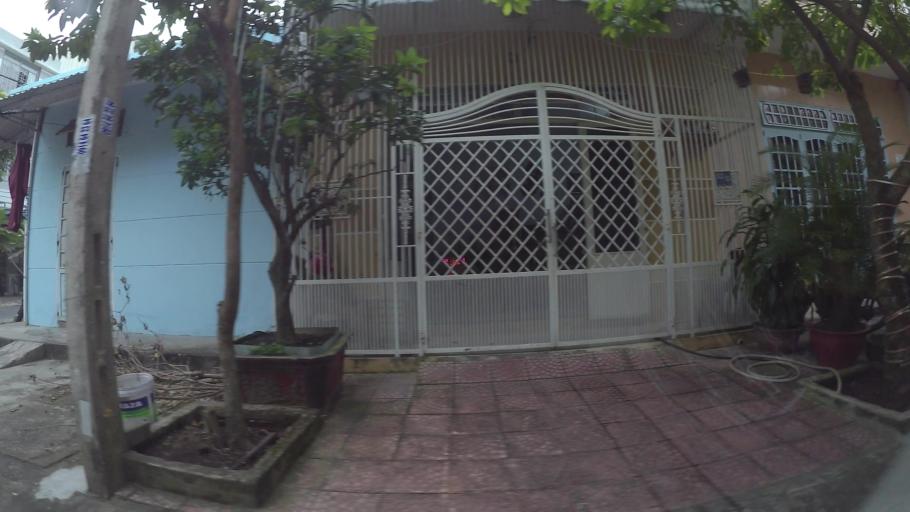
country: VN
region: Da Nang
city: Thanh Khe
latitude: 16.0577
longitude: 108.1872
